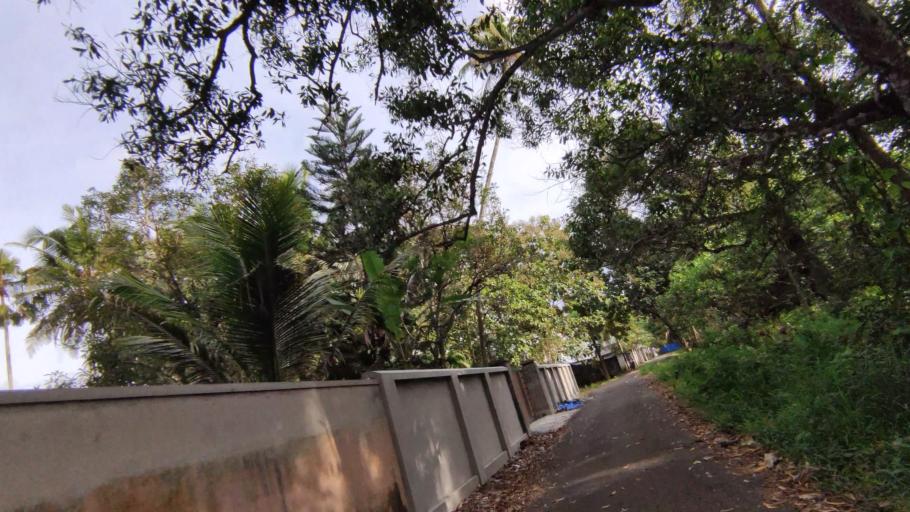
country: IN
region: Kerala
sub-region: Alappuzha
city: Shertallai
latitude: 9.6312
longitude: 76.3349
